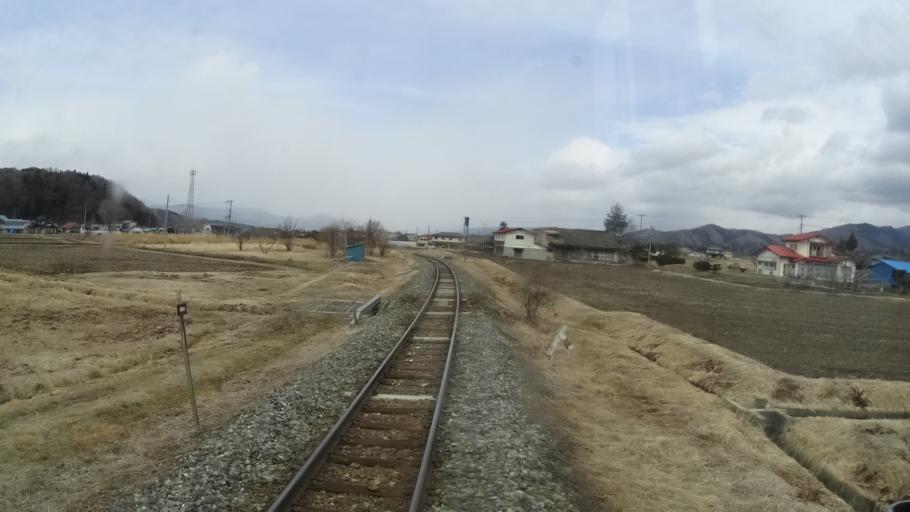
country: JP
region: Iwate
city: Tono
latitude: 39.2789
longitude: 141.5909
